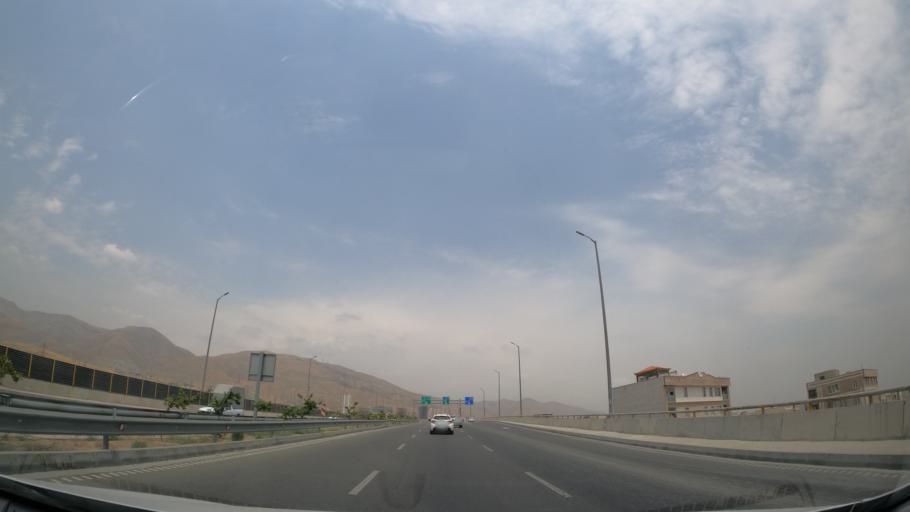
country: IR
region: Tehran
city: Shahr-e Qods
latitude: 35.7391
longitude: 51.1221
